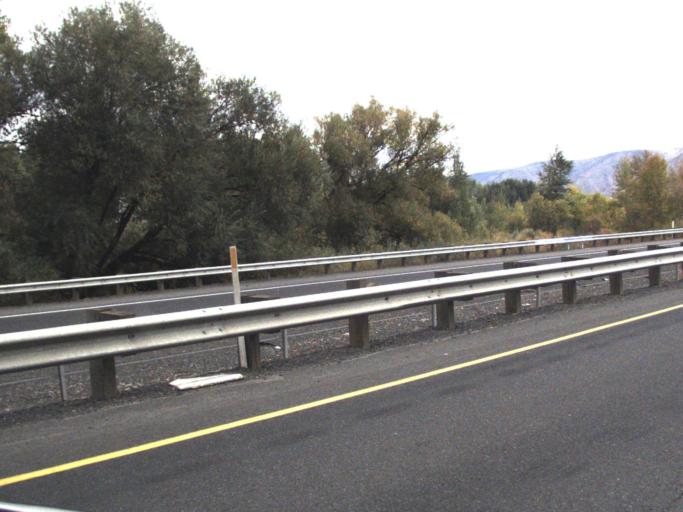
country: US
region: Washington
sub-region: Yakima County
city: Union Gap
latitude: 46.5576
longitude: -120.4706
